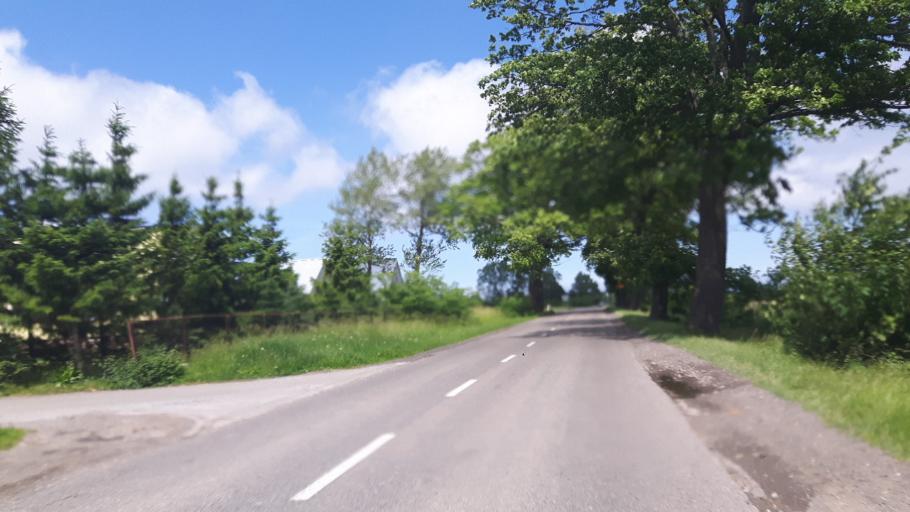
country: PL
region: Pomeranian Voivodeship
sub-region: Powiat slupski
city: Ustka
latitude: 54.5428
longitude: 16.8238
